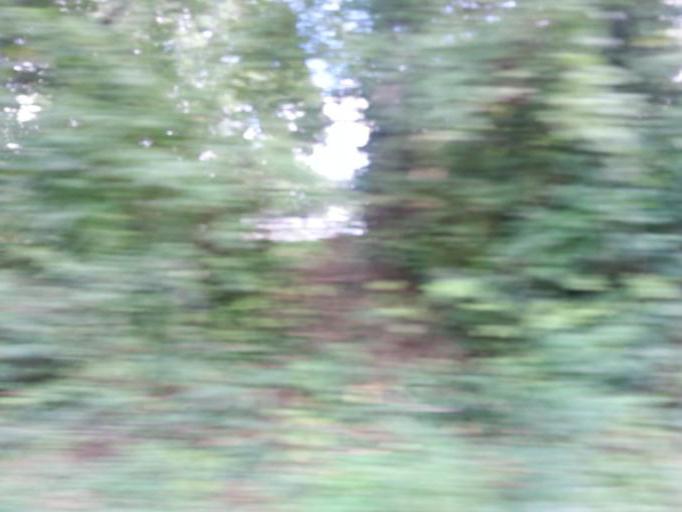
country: US
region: Tennessee
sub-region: Knox County
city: Knoxville
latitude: 36.0094
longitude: -83.9033
